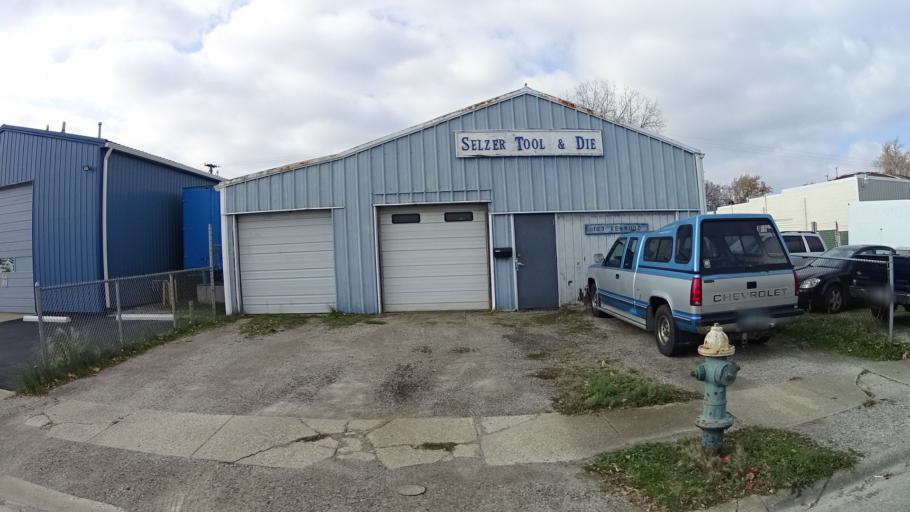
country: US
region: Ohio
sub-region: Lorain County
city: Elyria
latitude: 41.3739
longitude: -82.0816
